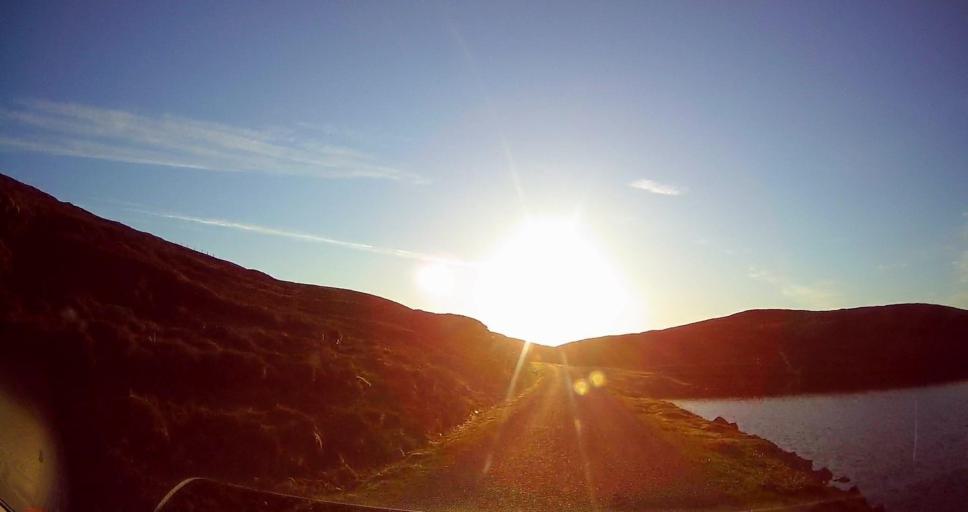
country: GB
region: Scotland
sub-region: Shetland Islands
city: Lerwick
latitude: 60.4438
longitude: -1.4085
